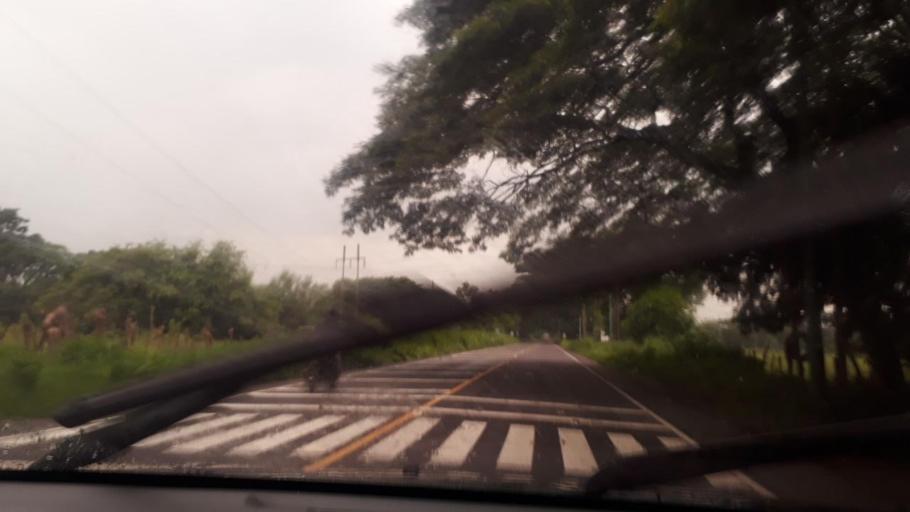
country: GT
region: Santa Rosa
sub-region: Municipio de Taxisco
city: Taxisco
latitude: 14.0950
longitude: -90.5766
